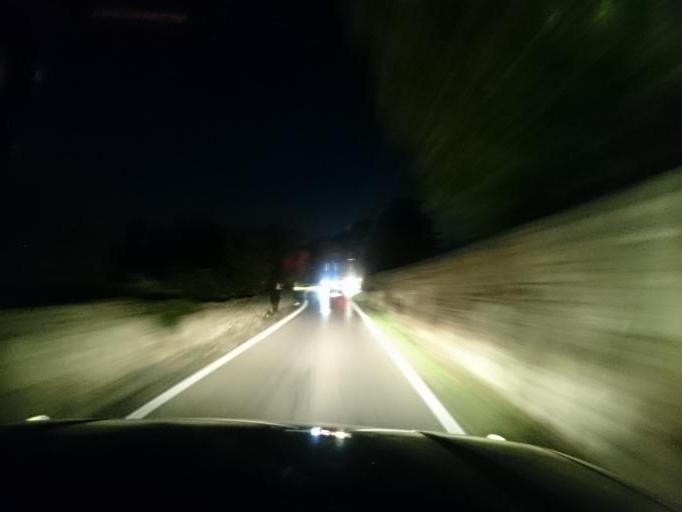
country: IT
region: Veneto
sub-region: Provincia di Padova
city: Baone
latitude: 45.2353
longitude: 11.6722
